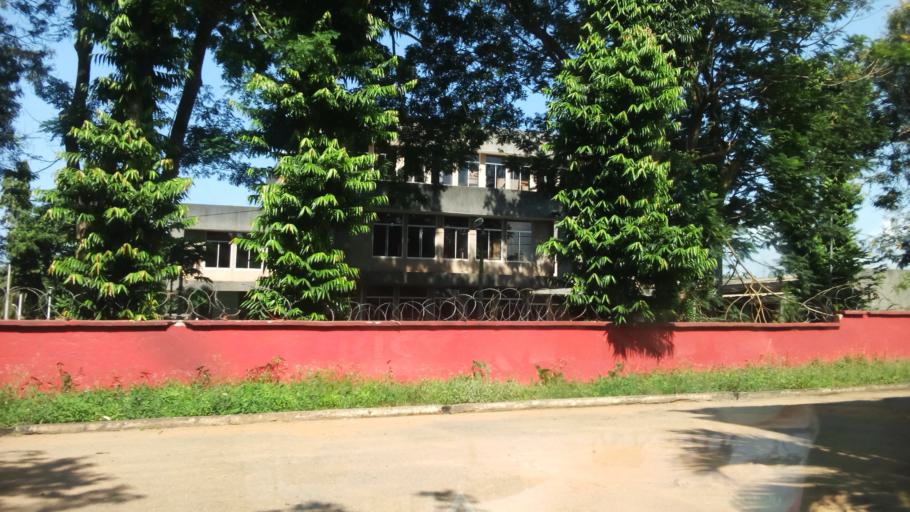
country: GH
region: Central
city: Cape Coast
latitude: 5.1215
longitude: -1.2730
